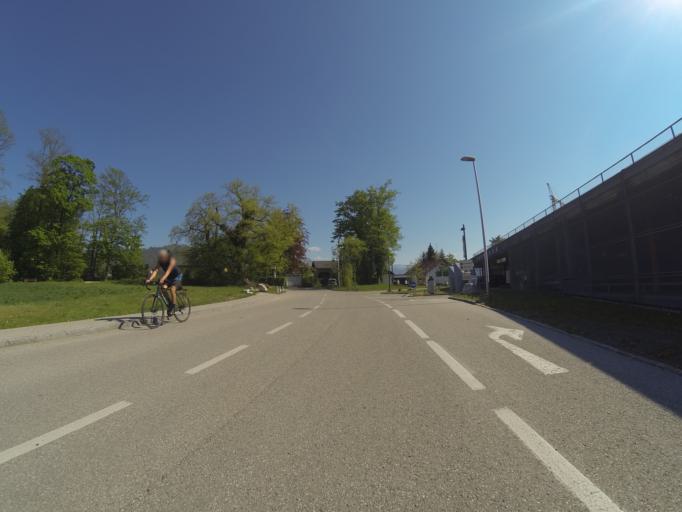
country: AT
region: Upper Austria
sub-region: Politischer Bezirk Gmunden
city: Gmunden
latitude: 47.9170
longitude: 13.7820
